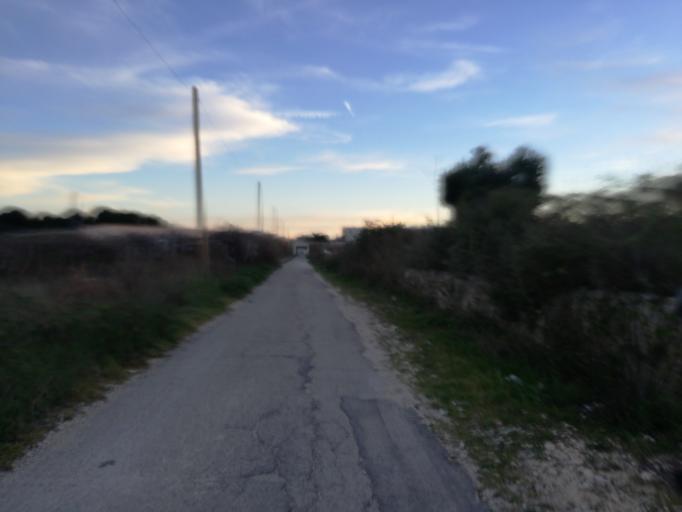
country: IT
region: Apulia
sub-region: Provincia di Bari
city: Adelfia
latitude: 41.0093
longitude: 16.8718
